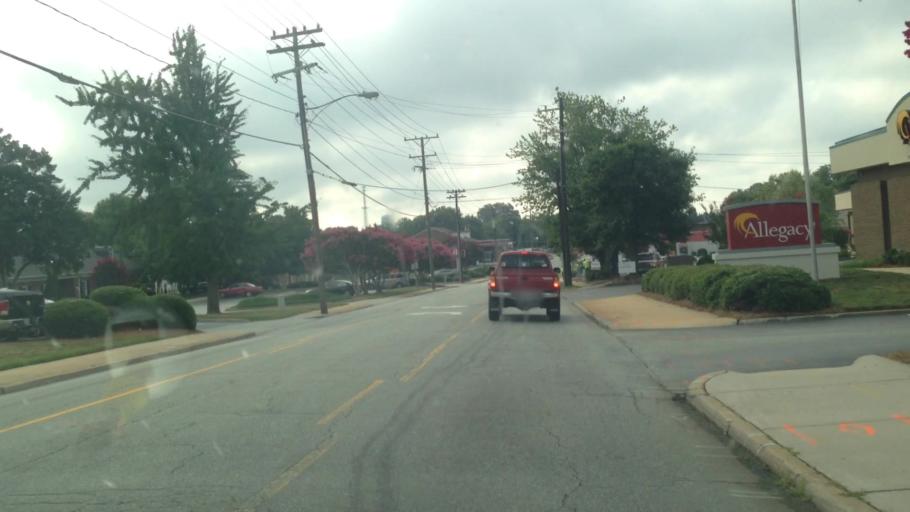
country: US
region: North Carolina
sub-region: Forsyth County
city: Kernersville
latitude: 36.1193
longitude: -80.0717
